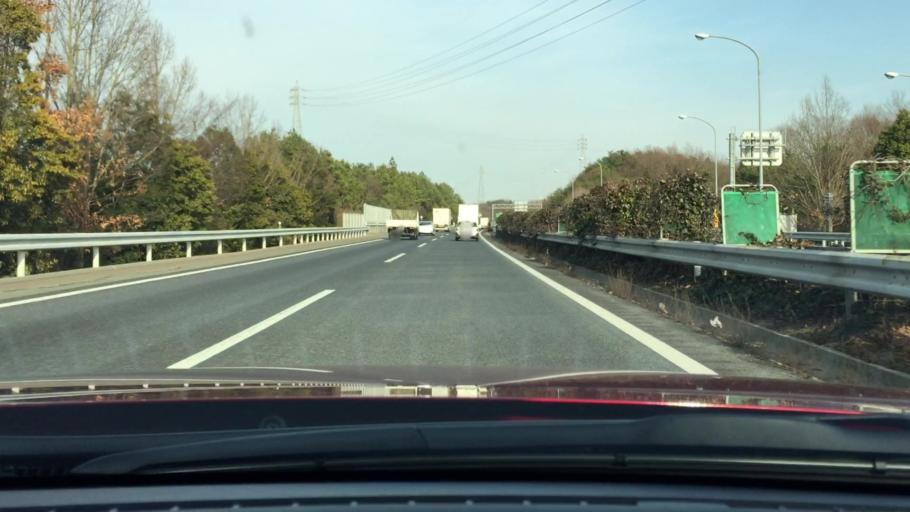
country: JP
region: Hyogo
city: Miki
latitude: 34.8142
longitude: 134.9610
